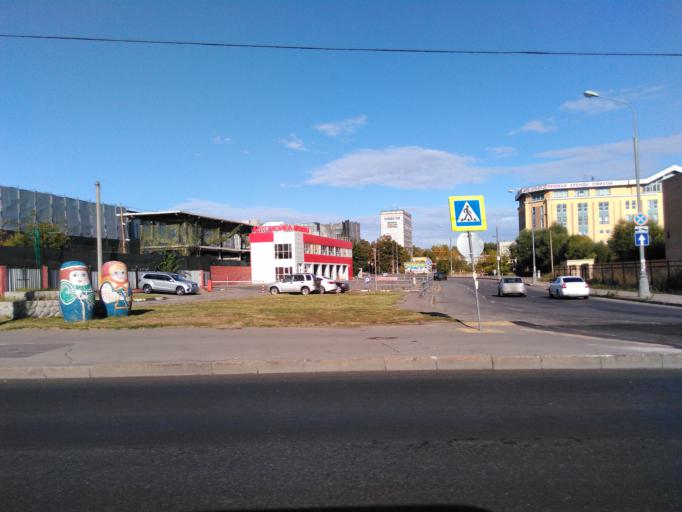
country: RU
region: Moscow
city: Likhobory
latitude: 55.8532
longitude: 37.5640
